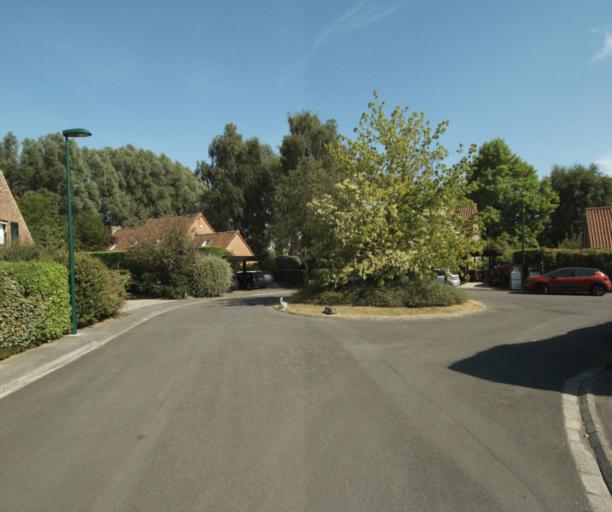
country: FR
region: Nord-Pas-de-Calais
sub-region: Departement du Nord
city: Bondues
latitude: 50.7093
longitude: 3.0737
